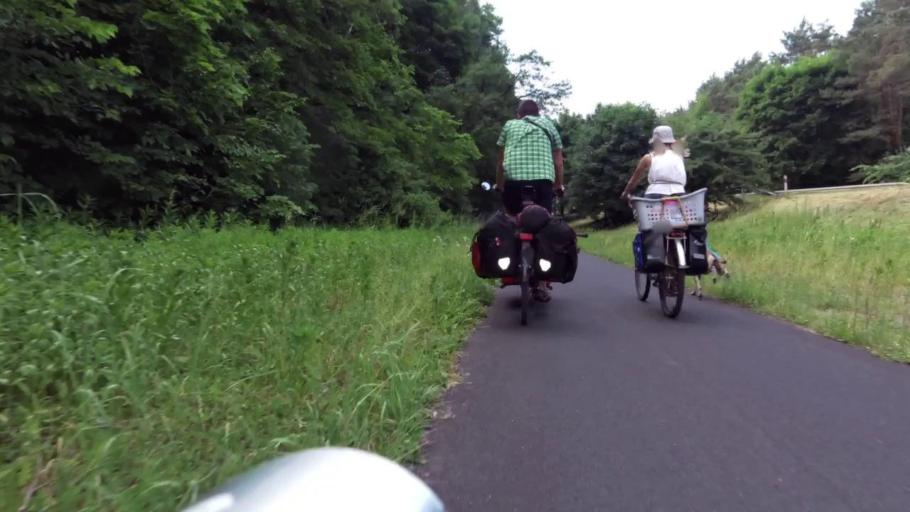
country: PL
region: Kujawsko-Pomorskie
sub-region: Powiat torunski
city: Lysomice
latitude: 53.0793
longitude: 18.5405
